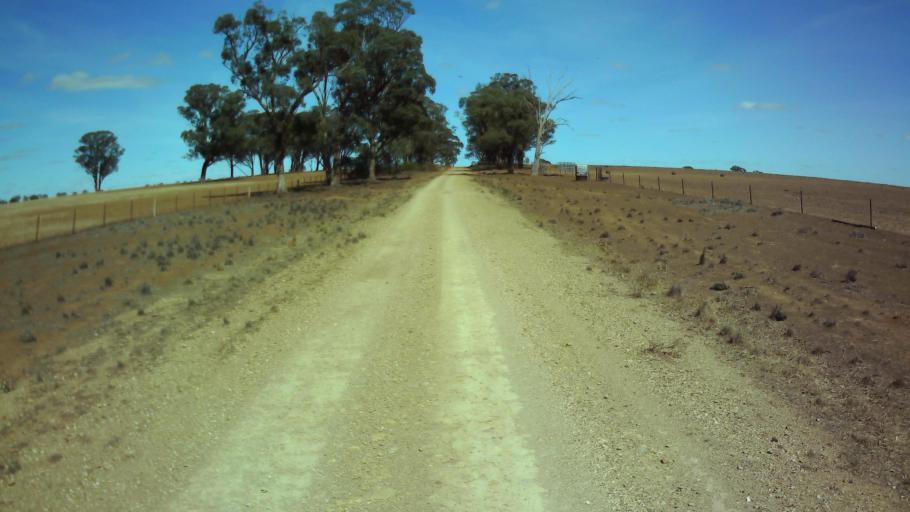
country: AU
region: New South Wales
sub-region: Weddin
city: Grenfell
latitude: -33.7253
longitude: 147.8693
